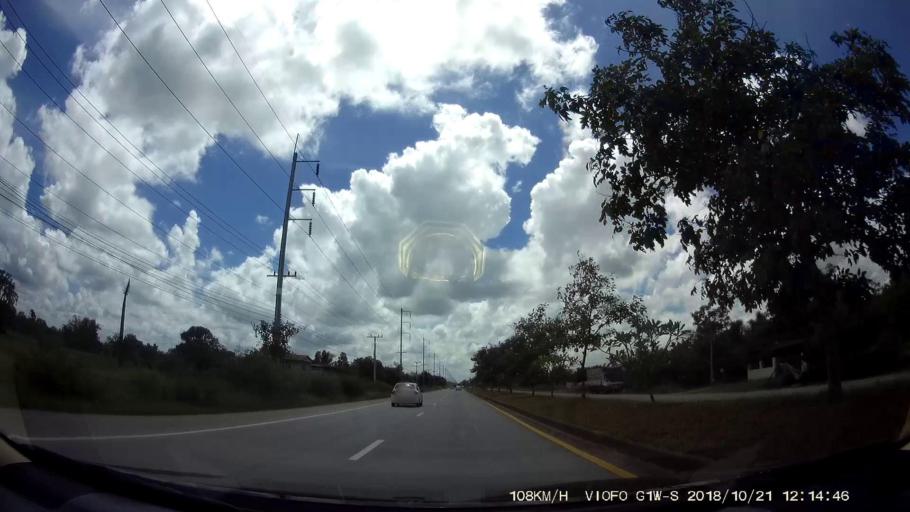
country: TH
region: Nakhon Ratchasima
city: Dan Khun Thot
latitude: 15.3721
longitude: 101.8335
